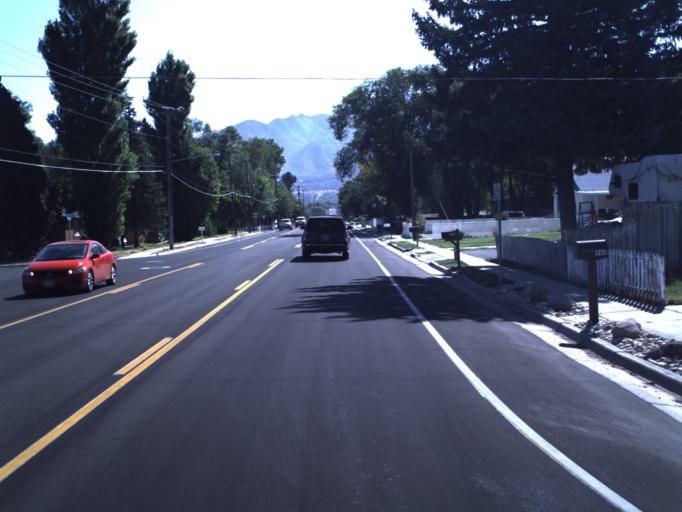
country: US
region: Utah
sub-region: Salt Lake County
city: Millcreek
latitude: 40.6743
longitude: -111.8639
